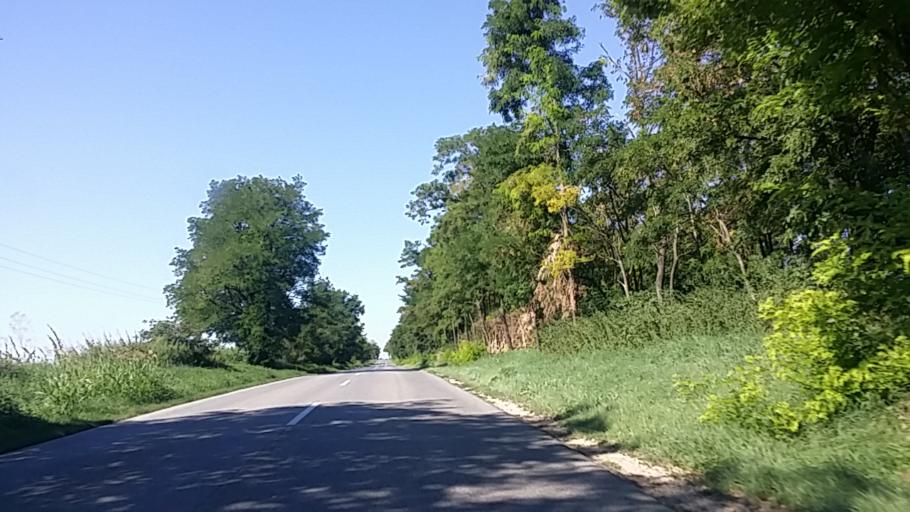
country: HU
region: Fejer
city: Mezofalva
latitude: 46.9015
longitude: 18.7174
